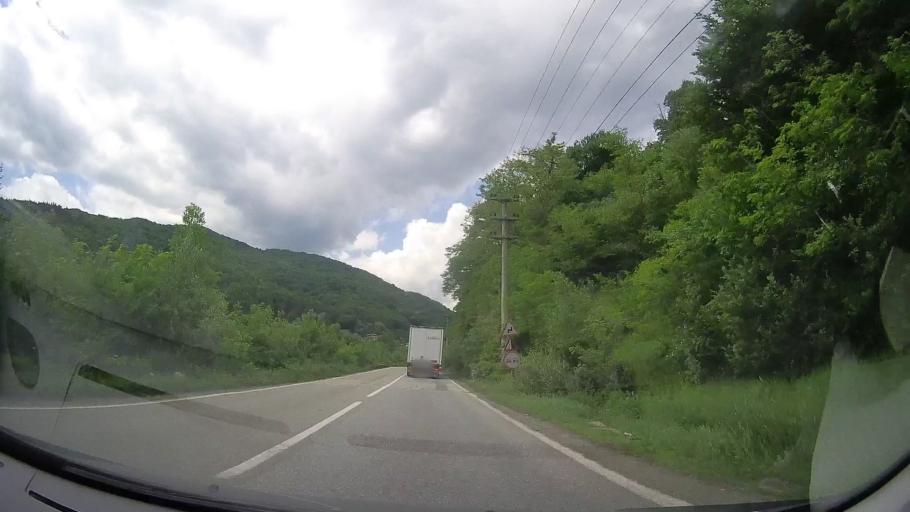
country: RO
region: Valcea
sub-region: Oras Calimanesti
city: Jiblea Veche
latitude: 45.2487
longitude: 24.3421
